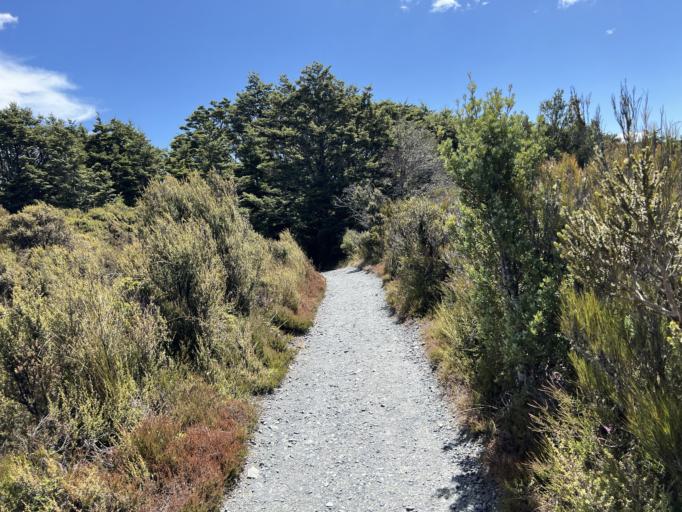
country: NZ
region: Manawatu-Wanganui
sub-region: Ruapehu District
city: Waiouru
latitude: -39.2003
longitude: 175.5497
